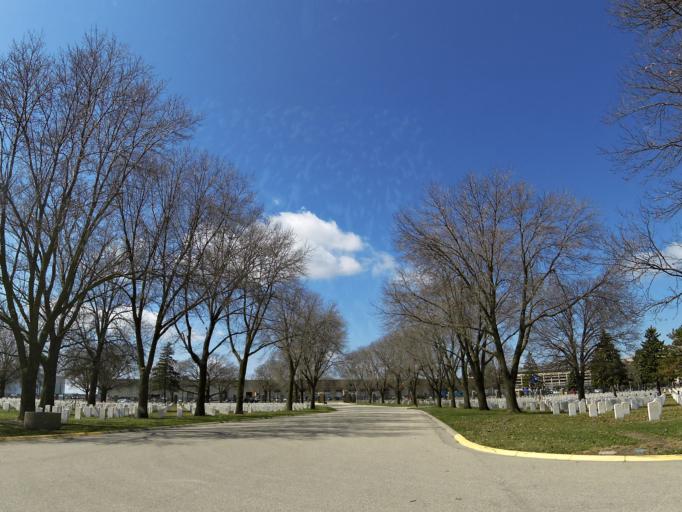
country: US
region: Minnesota
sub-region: Hennepin County
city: Richfield
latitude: 44.8700
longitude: -93.2209
